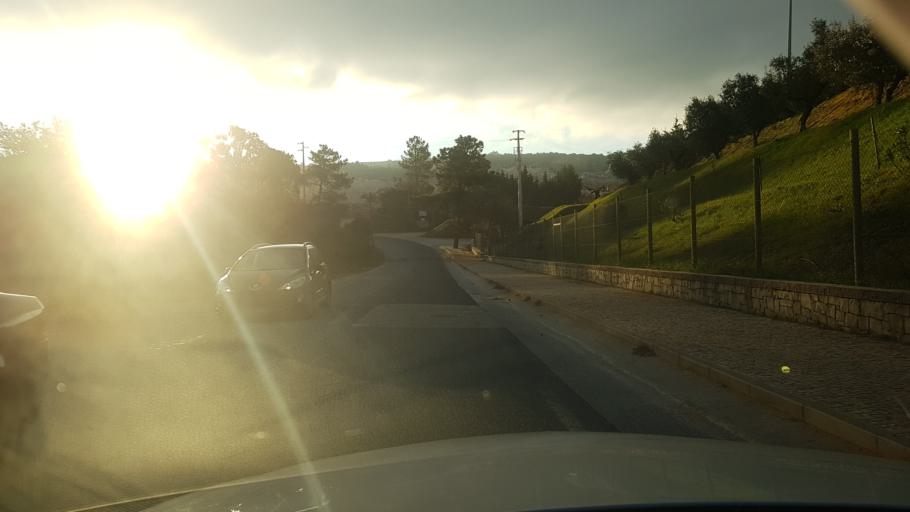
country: PT
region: Santarem
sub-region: Ourem
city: Fatima
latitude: 39.5752
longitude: -8.6141
